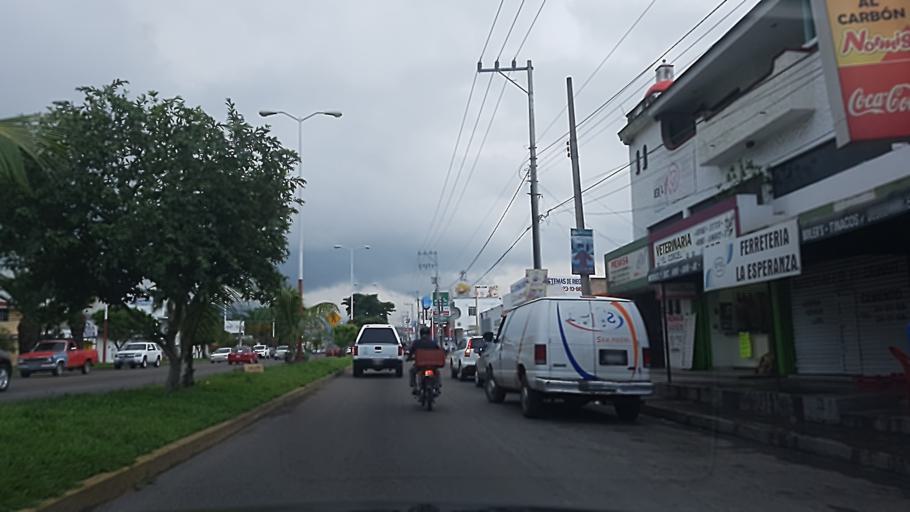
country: MX
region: Nayarit
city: Xalisco
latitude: 21.4613
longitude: -104.8921
